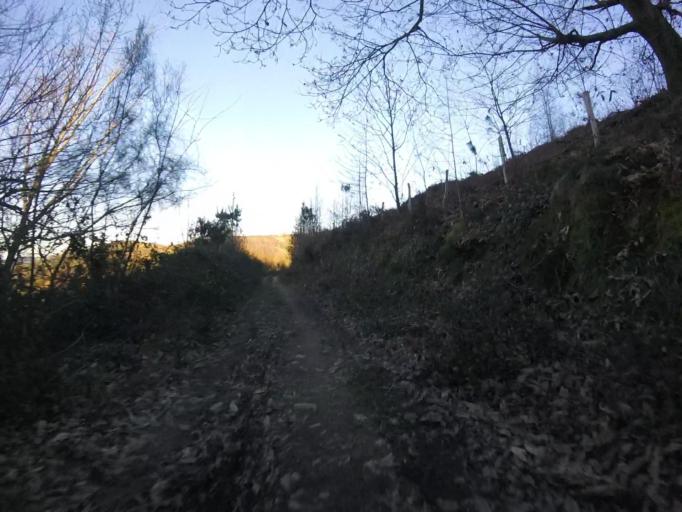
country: ES
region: Basque Country
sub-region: Provincia de Guipuzcoa
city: Errenteria
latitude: 43.2594
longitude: -1.8385
